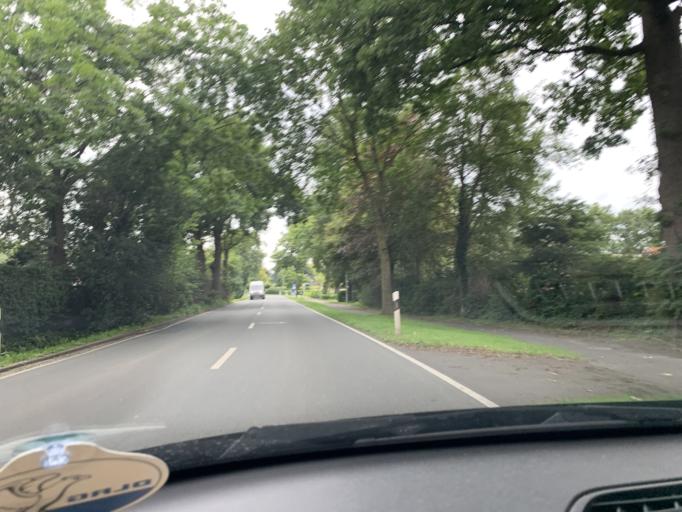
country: DE
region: Lower Saxony
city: Apen
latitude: 53.1738
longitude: 7.8288
